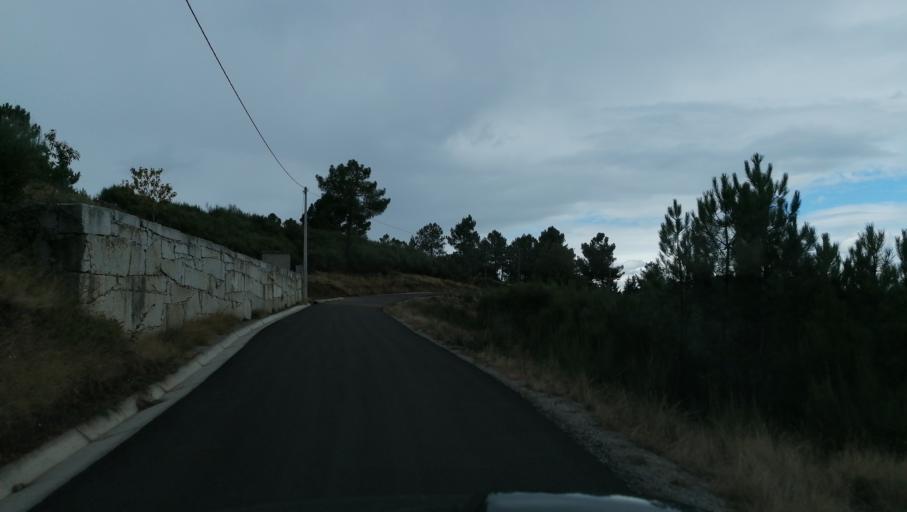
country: PT
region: Vila Real
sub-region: Vila Pouca de Aguiar
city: Vila Pouca de Aguiar
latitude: 41.5621
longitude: -7.6607
